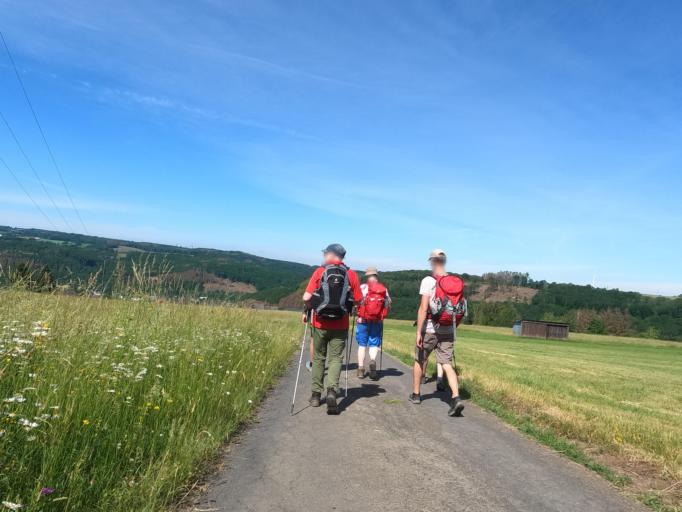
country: DE
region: Rheinland-Pfalz
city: Bolsberg
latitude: 50.6611
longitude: 7.9082
